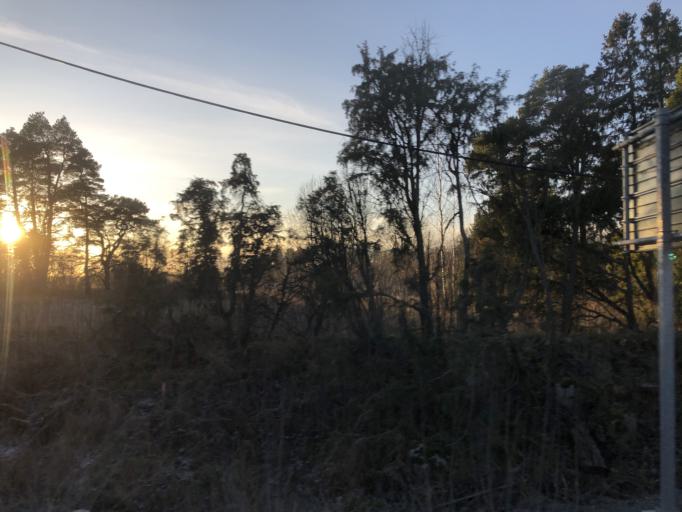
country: SE
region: Stockholm
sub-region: Jarfalla Kommun
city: Jakobsberg
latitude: 59.4104
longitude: 17.8849
